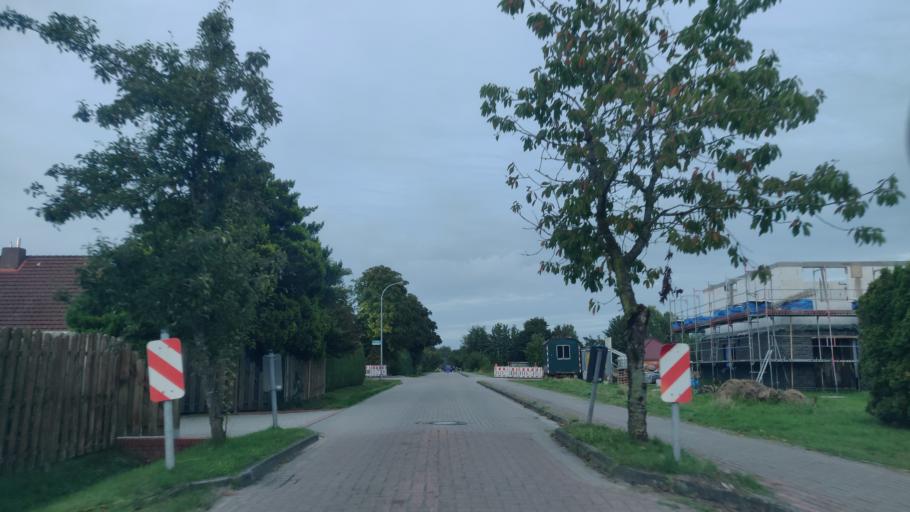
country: DE
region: Lower Saxony
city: Aurich
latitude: 53.4815
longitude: 7.4063
